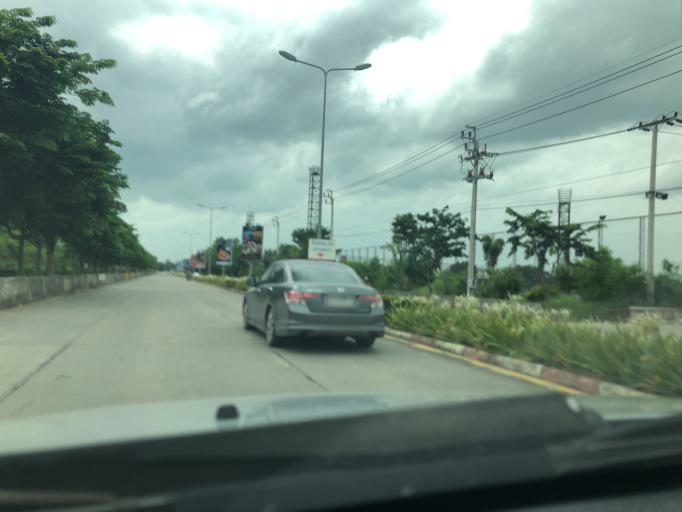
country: TH
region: Nonthaburi
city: Pak Kret
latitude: 13.9280
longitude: 100.5415
